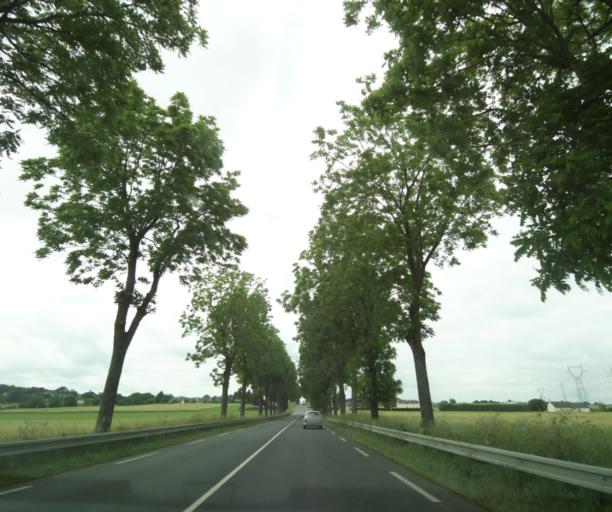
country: FR
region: Pays de la Loire
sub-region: Departement de Maine-et-Loire
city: Distre
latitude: 47.2029
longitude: -0.1217
